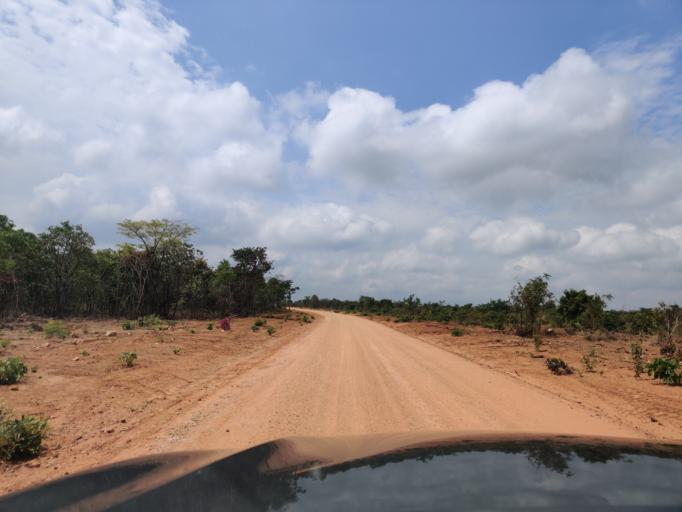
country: ZM
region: Central
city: Mkushi
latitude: -13.6635
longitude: 29.7513
